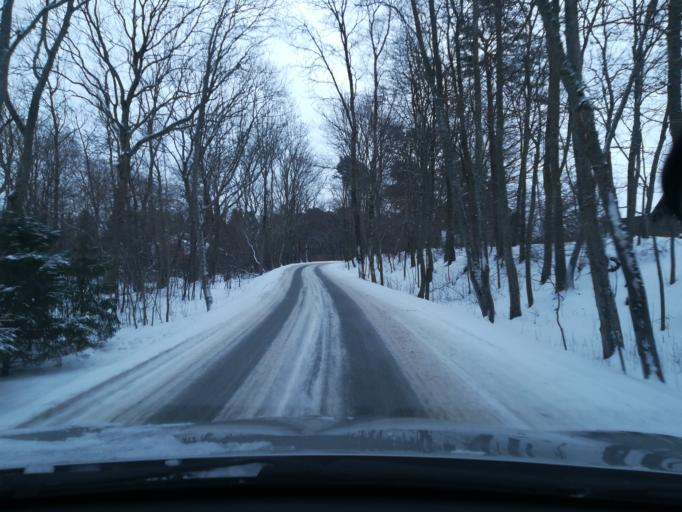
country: EE
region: Harju
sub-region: Harku vald
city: Tabasalu
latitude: 59.4480
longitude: 24.4914
